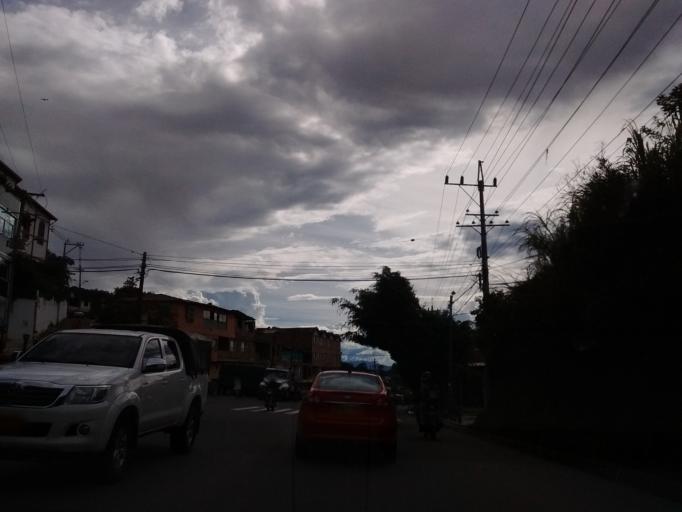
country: CO
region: Antioquia
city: Santuario
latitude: 6.1352
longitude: -75.2666
